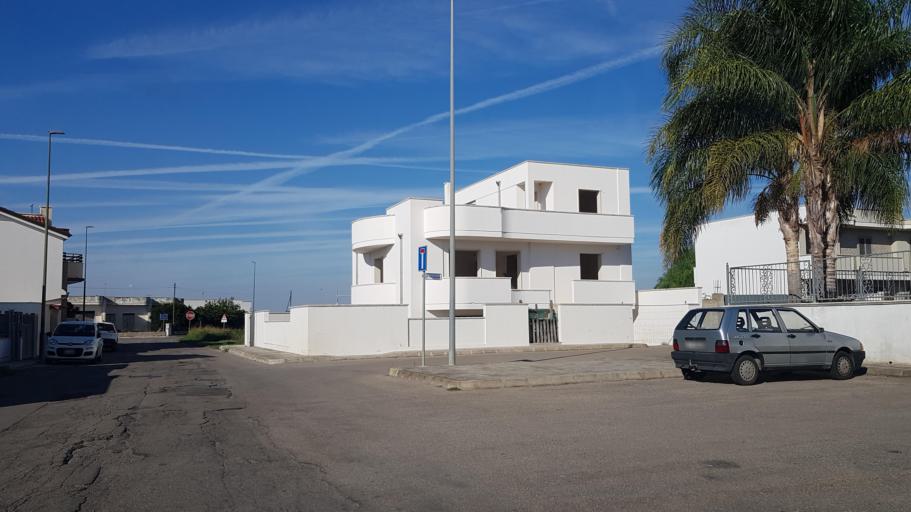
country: IT
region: Apulia
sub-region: Provincia di Lecce
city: Guagnano
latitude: 40.4044
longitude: 17.9525
